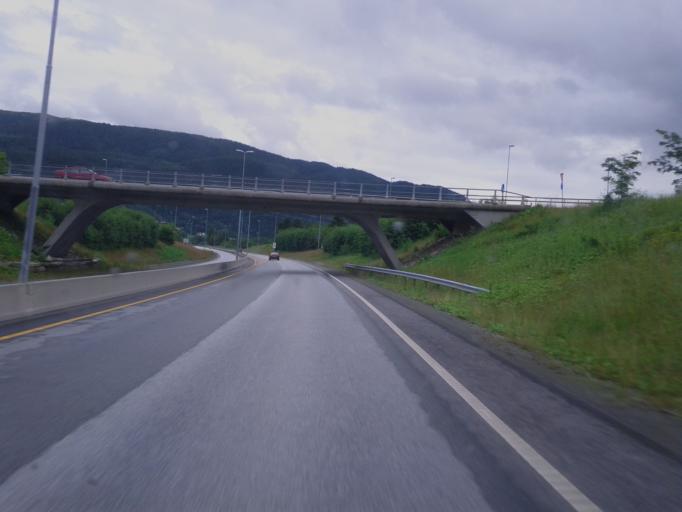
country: NO
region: Sor-Trondelag
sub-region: Melhus
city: Melhus
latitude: 63.2818
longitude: 10.2745
